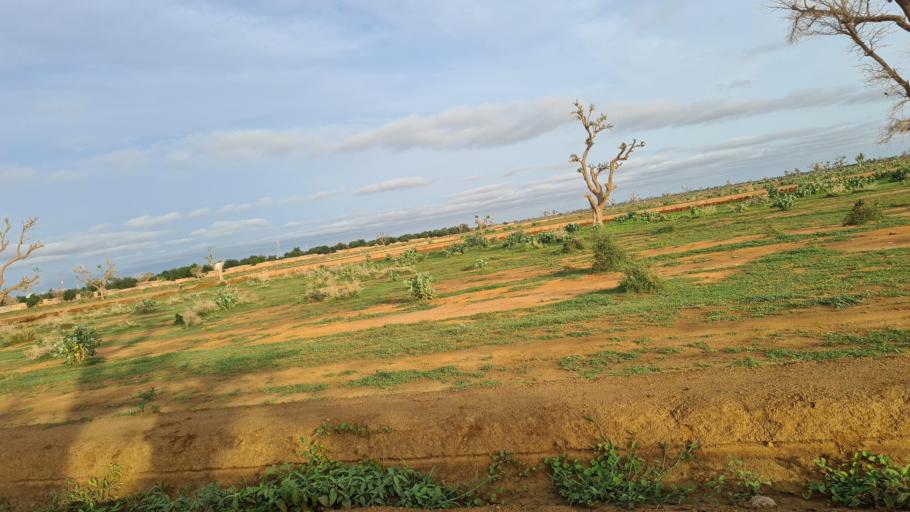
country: NE
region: Tahoua
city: Birni N Konni
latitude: 13.7886
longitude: 5.2348
